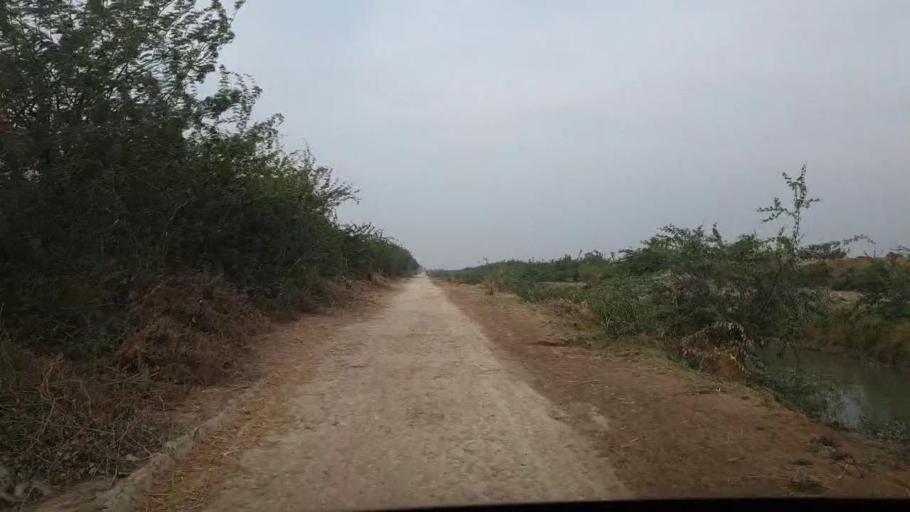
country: PK
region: Sindh
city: Chuhar Jamali
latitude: 24.4072
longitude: 67.9537
